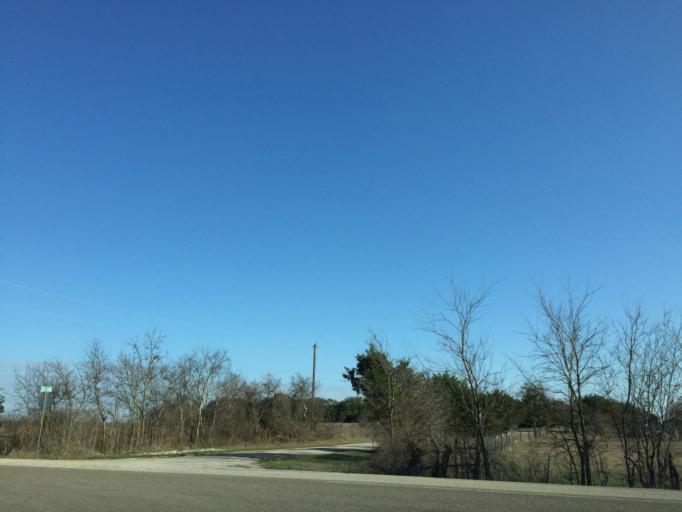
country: US
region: Texas
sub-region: Williamson County
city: Florence
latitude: 30.7686
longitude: -97.8309
